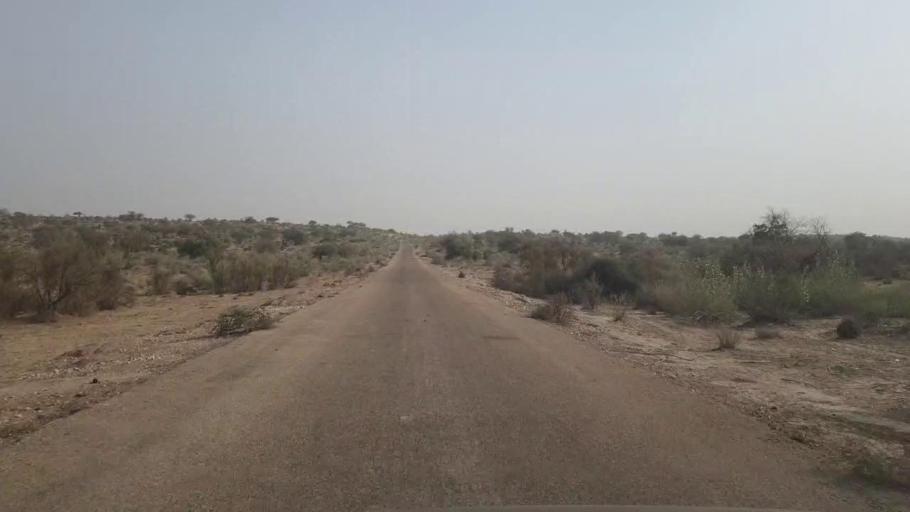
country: PK
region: Sindh
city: Chor
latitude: 25.4872
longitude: 69.9733
